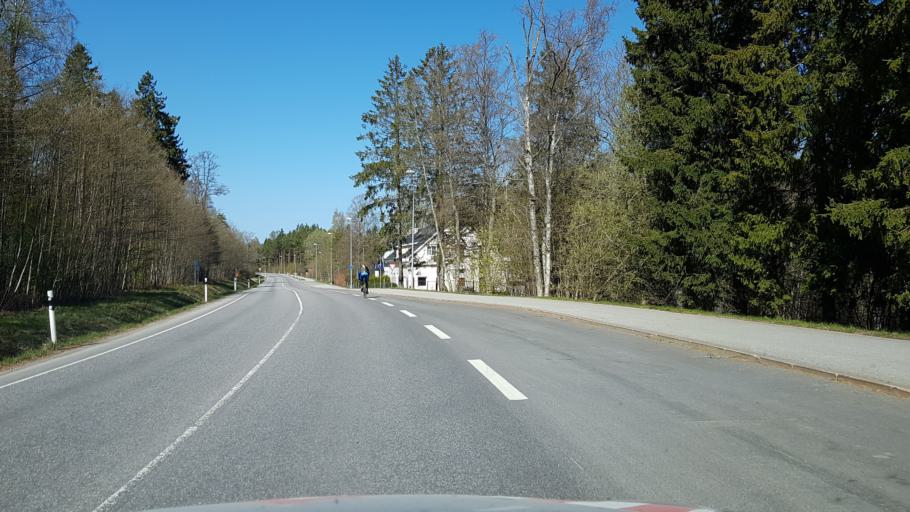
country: EE
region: Harju
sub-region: Viimsi vald
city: Viimsi
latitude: 59.5303
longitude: 24.8761
